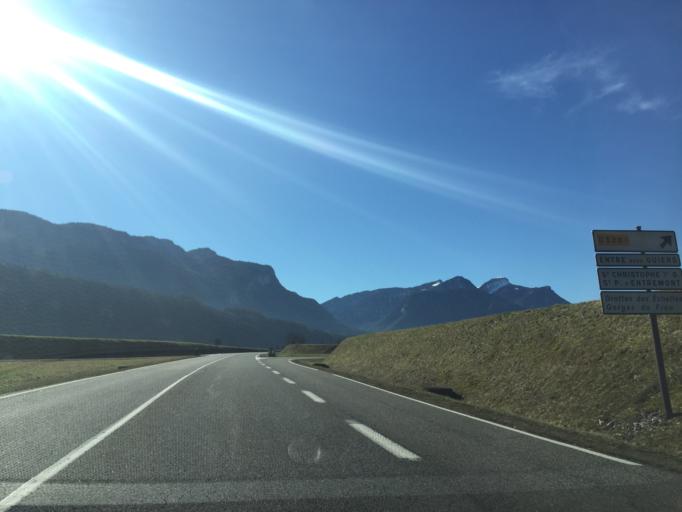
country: FR
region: Rhone-Alpes
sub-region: Departement de la Savoie
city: Les Echelles
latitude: 45.4364
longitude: 5.7656
